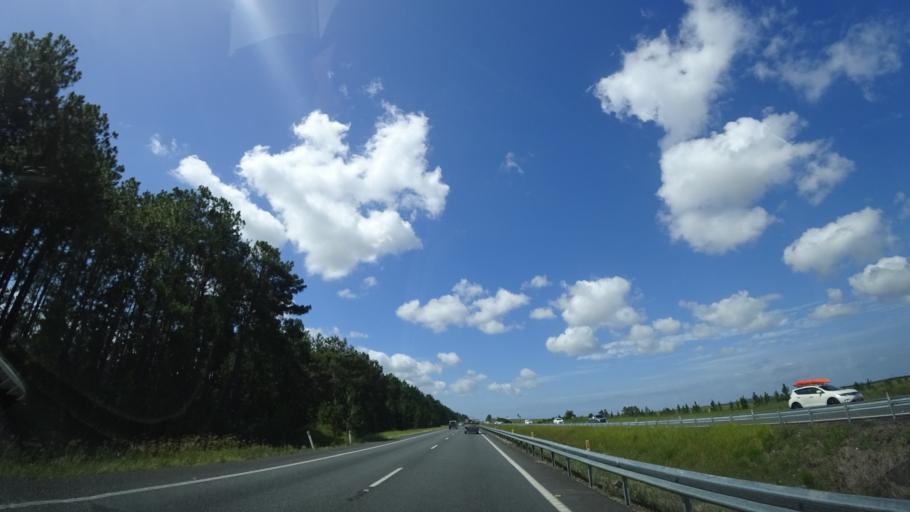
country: AU
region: Queensland
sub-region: Sunshine Coast
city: Little Mountain
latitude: -26.8321
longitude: 153.0334
